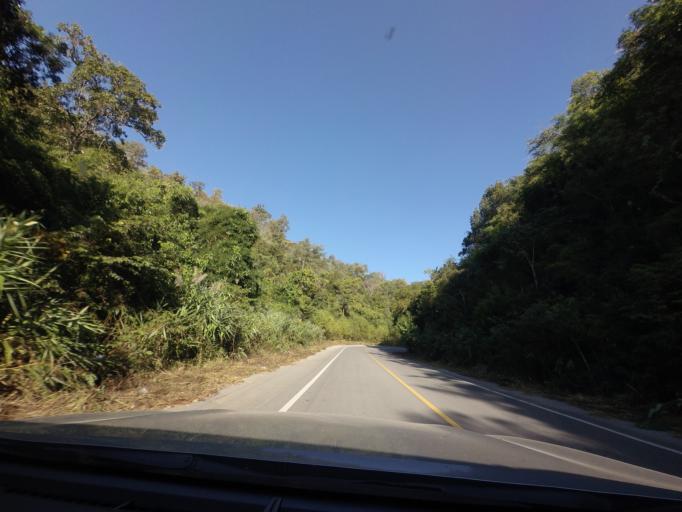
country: TH
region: Lampang
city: Chae Hom
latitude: 18.5523
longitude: 99.6287
